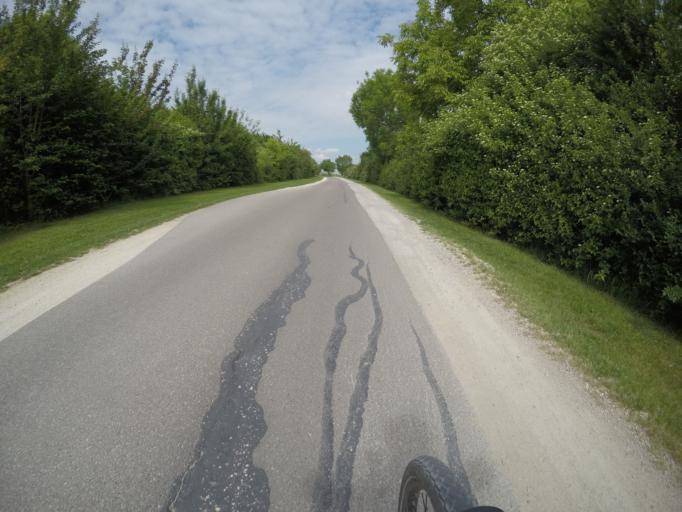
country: DE
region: Baden-Wuerttemberg
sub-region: Regierungsbezirk Stuttgart
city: Wernau
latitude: 48.6701
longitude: 9.4274
